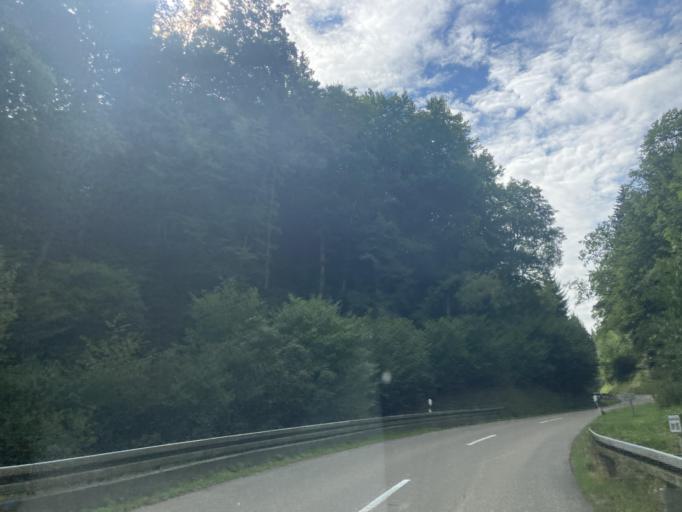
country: DE
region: Bavaria
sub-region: Swabia
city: Forheim
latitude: 48.7761
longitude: 10.4651
